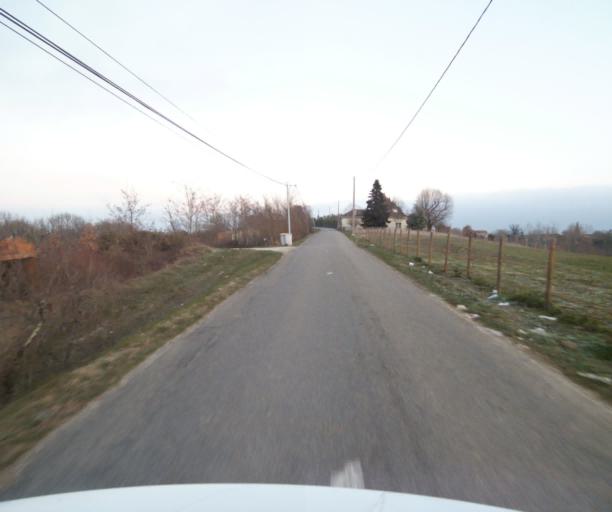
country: FR
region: Midi-Pyrenees
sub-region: Departement du Tarn-et-Garonne
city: Moissac
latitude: 44.1215
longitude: 1.0838
